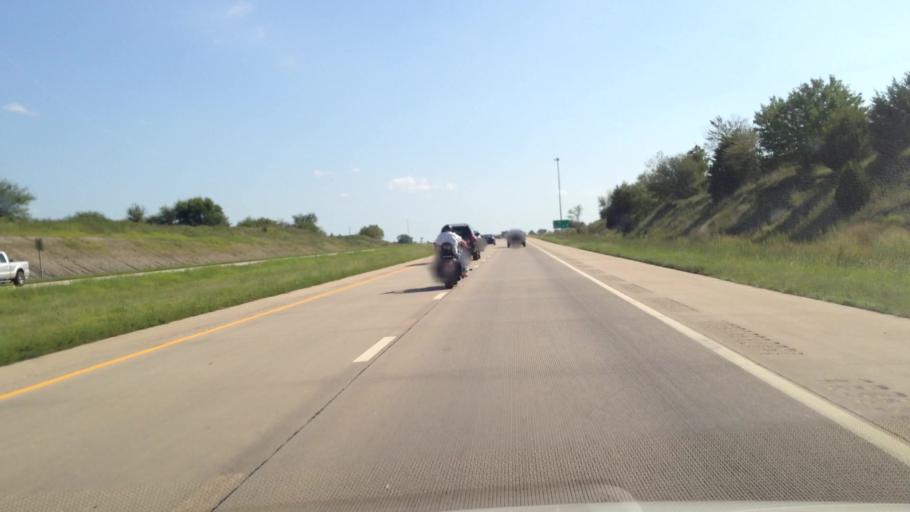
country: US
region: Kansas
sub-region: Bourbon County
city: Fort Scott
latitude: 38.0007
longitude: -94.7048
